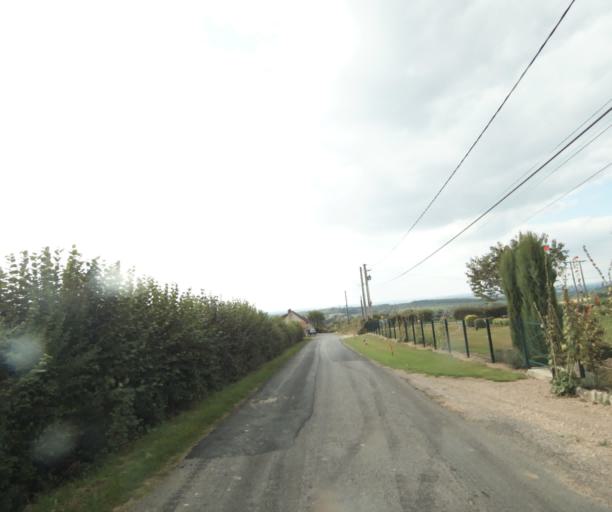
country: FR
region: Bourgogne
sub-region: Departement de Saone-et-Loire
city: Palinges
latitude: 46.5263
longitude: 4.2850
